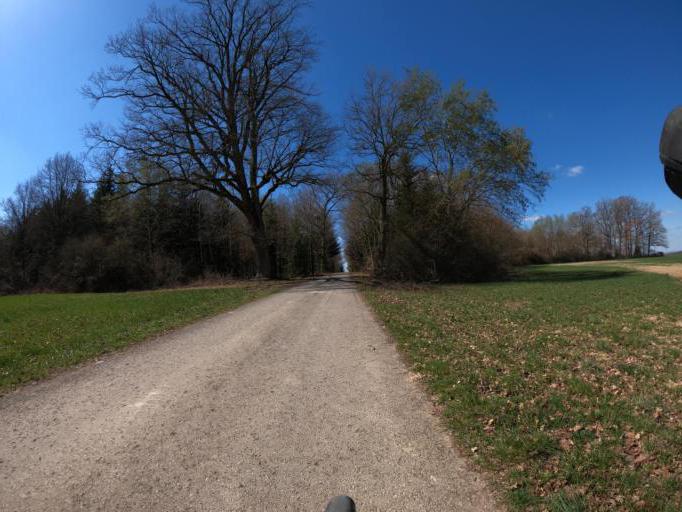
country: DE
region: Baden-Wuerttemberg
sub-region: Tuebingen Region
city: Haigerloch
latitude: 48.4227
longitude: 8.8001
